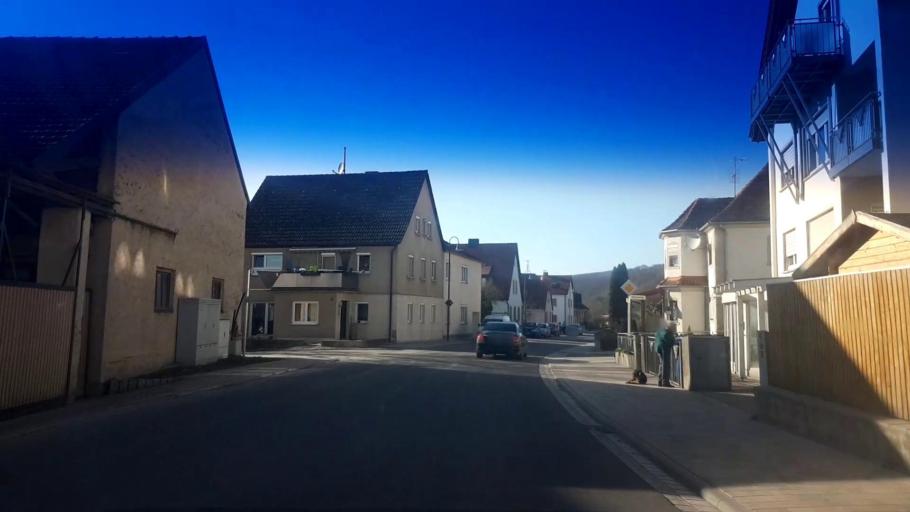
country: DE
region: Bavaria
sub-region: Regierungsbezirk Unterfranken
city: Stettfeld
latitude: 49.9702
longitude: 10.7204
